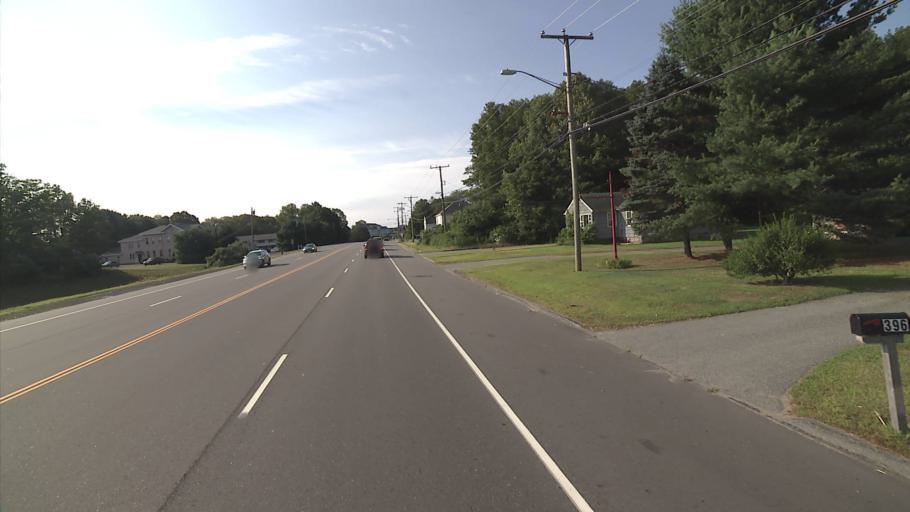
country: US
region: Connecticut
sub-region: New London County
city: Pawcatuck
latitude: 41.4012
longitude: -71.8470
